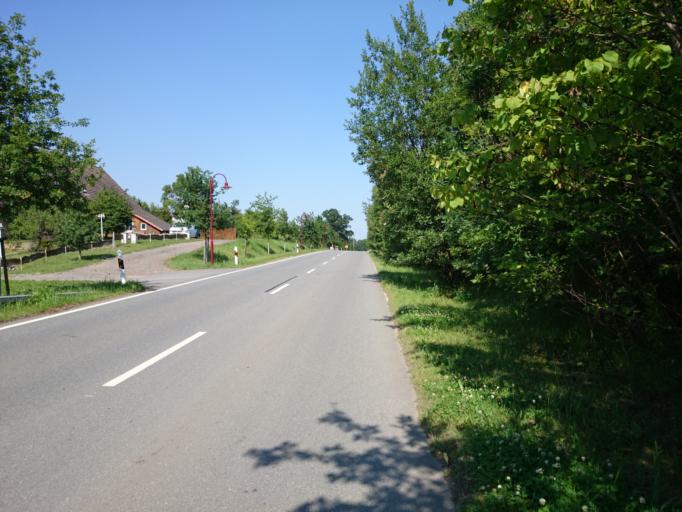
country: DE
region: Mecklenburg-Vorpommern
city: Tessin
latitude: 54.0433
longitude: 12.3975
